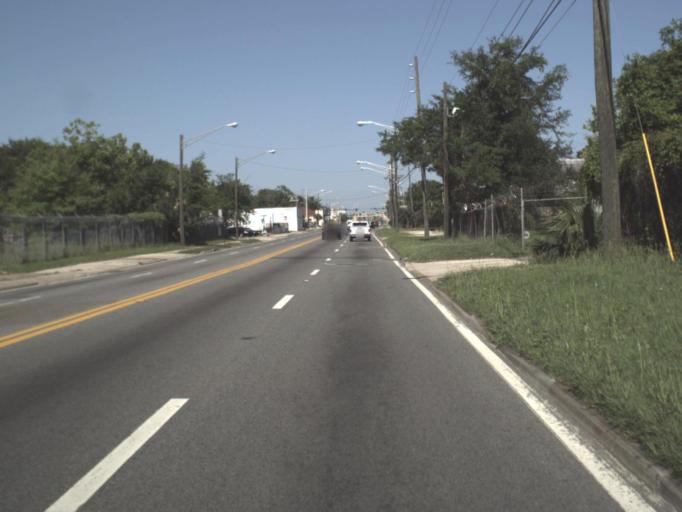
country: US
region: Florida
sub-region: Duval County
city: Jacksonville
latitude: 30.3333
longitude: -81.6958
